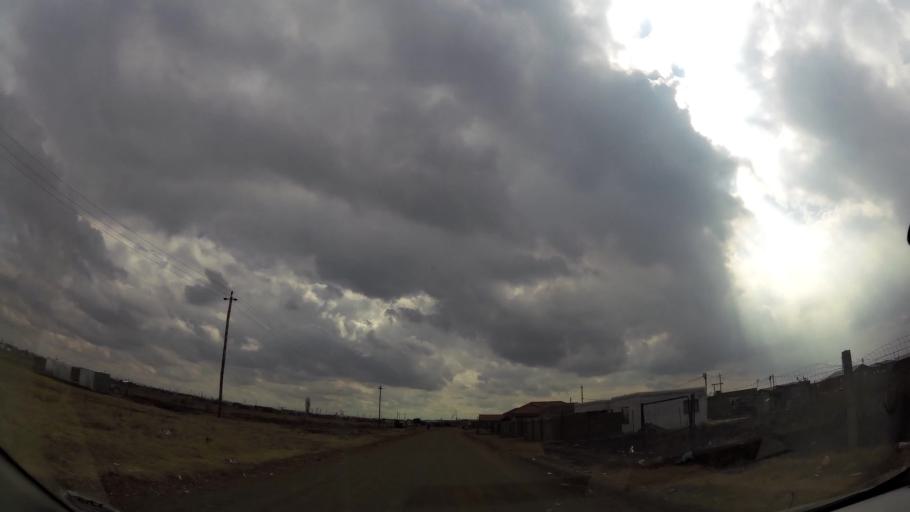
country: ZA
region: Orange Free State
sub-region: Fezile Dabi District Municipality
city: Sasolburg
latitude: -26.8540
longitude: 27.8980
